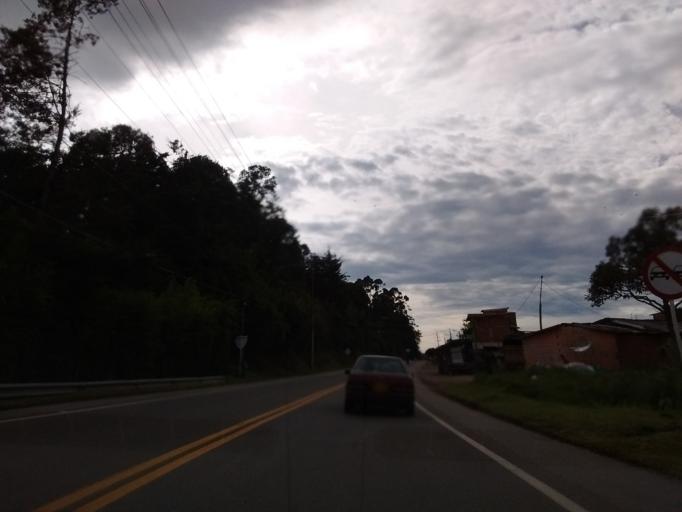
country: CO
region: Antioquia
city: Santuario
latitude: 6.1312
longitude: -75.2583
